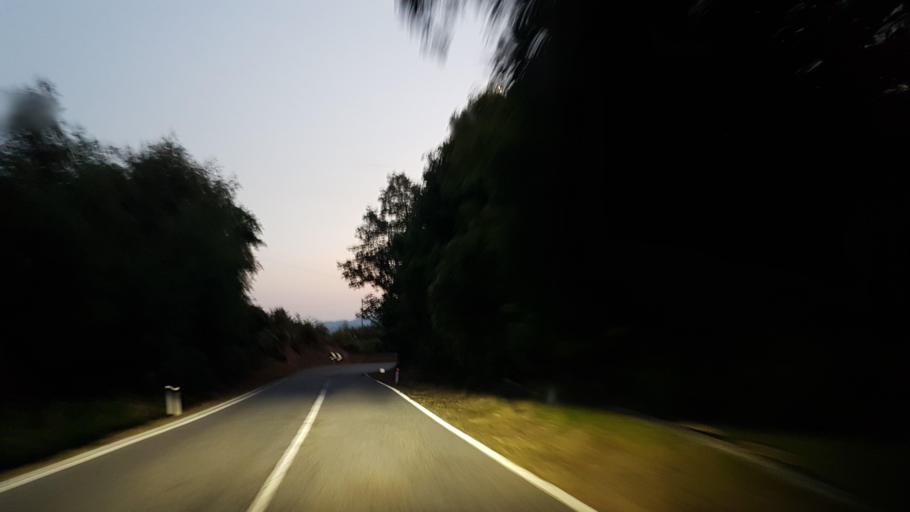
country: IT
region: Liguria
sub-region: Provincia di La Spezia
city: Varese Ligure
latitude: 44.3904
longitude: 9.6164
